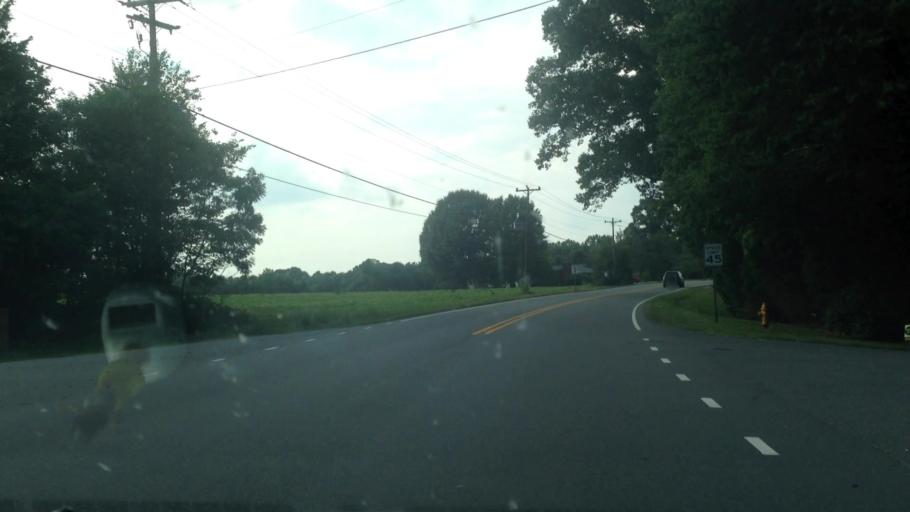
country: US
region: North Carolina
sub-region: Forsyth County
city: Walkertown
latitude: 36.1444
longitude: -80.1274
